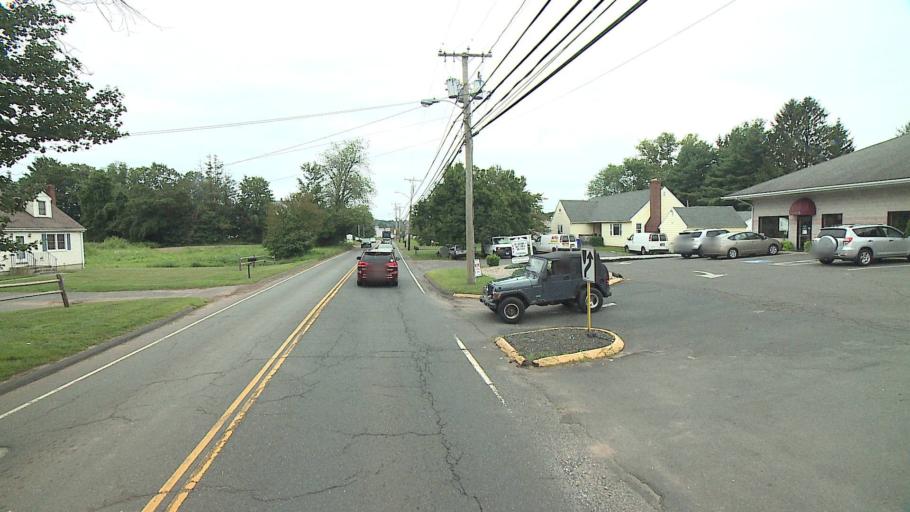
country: US
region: Connecticut
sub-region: Middlesex County
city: Cromwell
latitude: 41.5829
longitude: -72.6731
